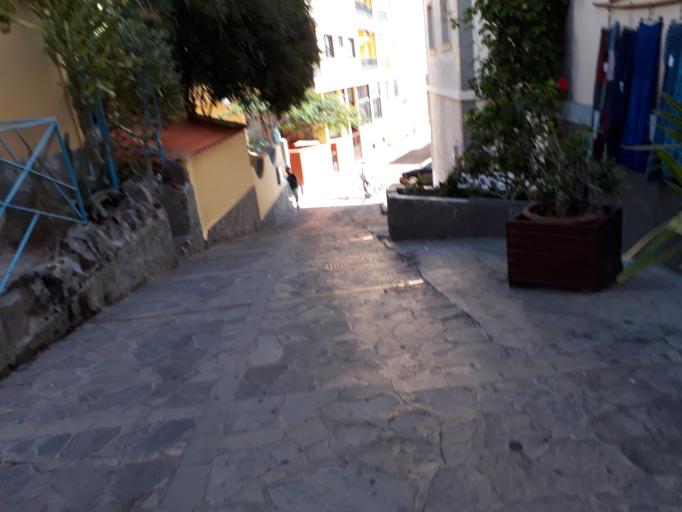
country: ES
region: Canary Islands
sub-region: Provincia de Santa Cruz de Tenerife
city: Alajero
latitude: 28.0830
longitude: -17.3348
